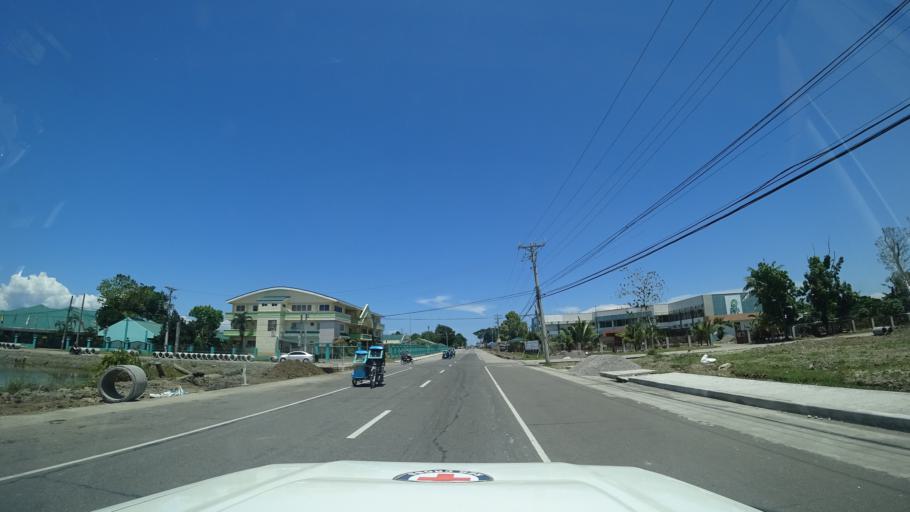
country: PH
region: Eastern Visayas
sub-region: Province of Leyte
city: Pawing
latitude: 11.1755
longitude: 125.0078
